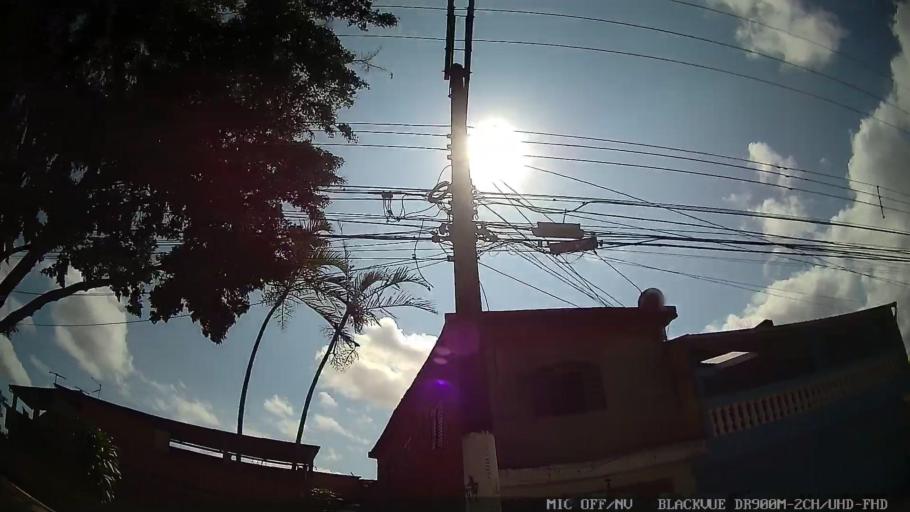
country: BR
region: Sao Paulo
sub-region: Guarulhos
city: Guarulhos
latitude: -23.4924
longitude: -46.4711
